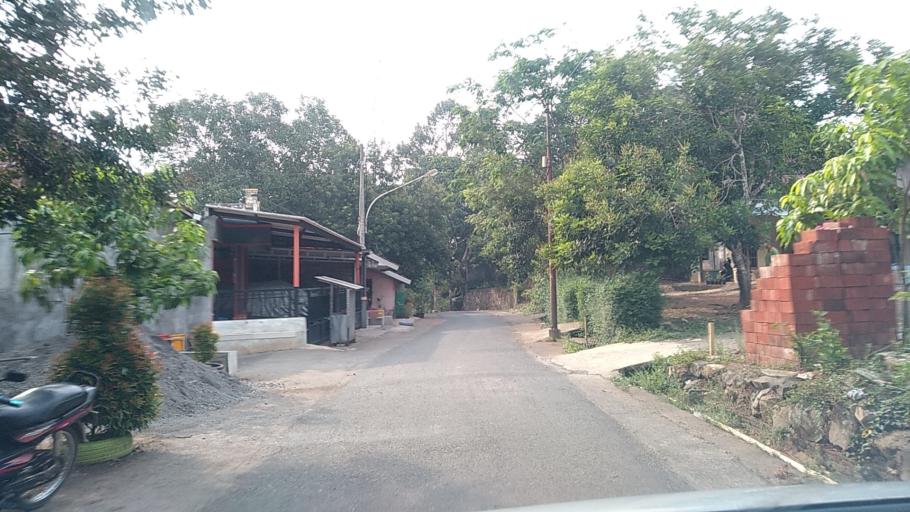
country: ID
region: Central Java
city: Ungaran
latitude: -7.0854
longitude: 110.3887
